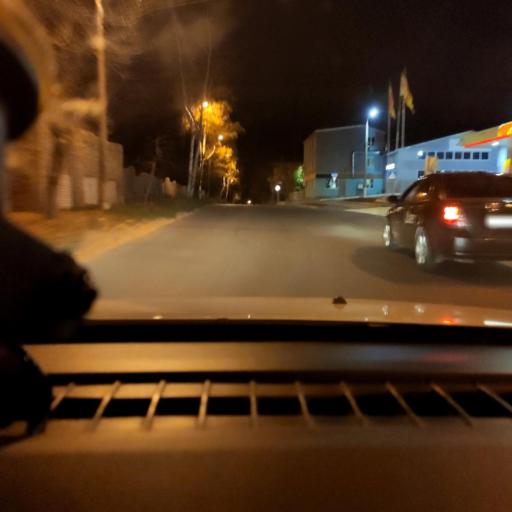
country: RU
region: Samara
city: Rozhdestveno
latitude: 53.1767
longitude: 50.0798
